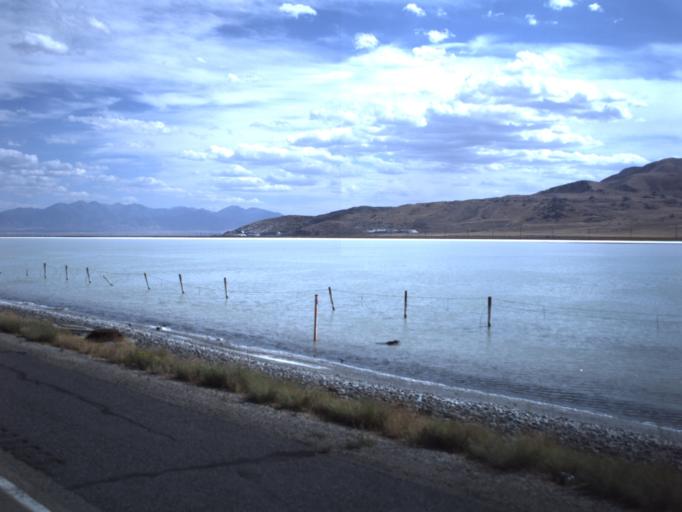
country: US
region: Utah
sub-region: Tooele County
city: Grantsville
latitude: 40.7363
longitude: -112.6110
